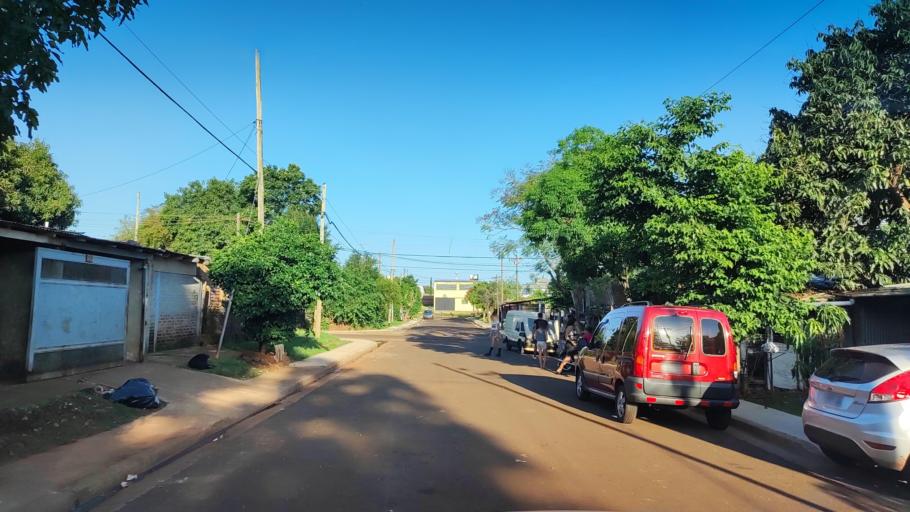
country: AR
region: Misiones
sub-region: Departamento de Capital
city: Posadas
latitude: -27.3829
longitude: -55.9277
